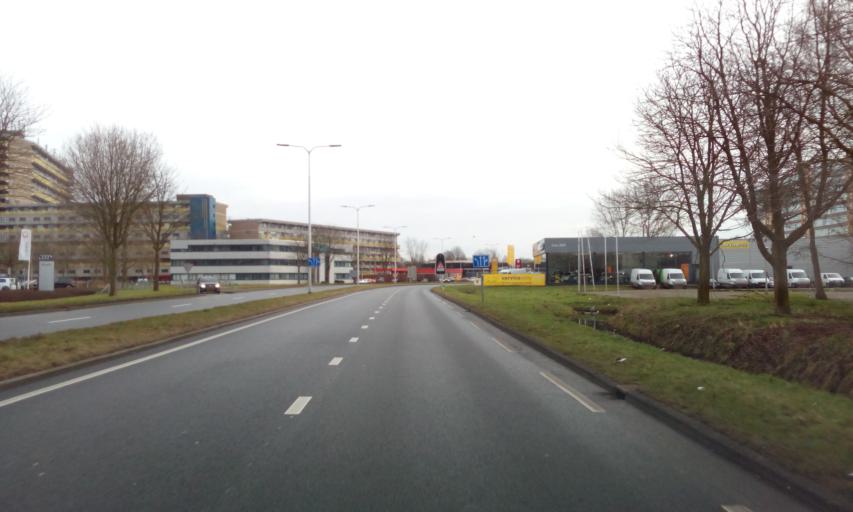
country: NL
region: South Holland
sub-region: Gemeente Gorinchem
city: Gorinchem
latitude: 51.8428
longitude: 4.9497
